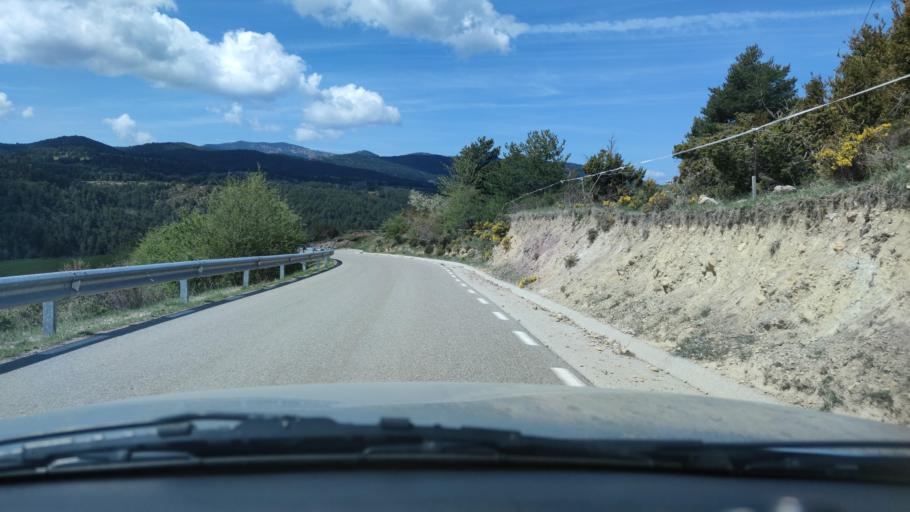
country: ES
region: Catalonia
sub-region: Provincia de Lleida
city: Coll de Nargo
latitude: 42.2824
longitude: 1.2242
